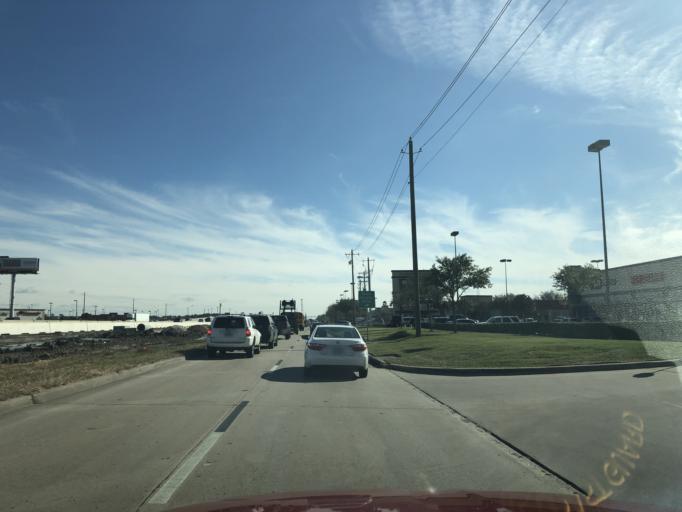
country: US
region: Texas
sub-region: Galveston County
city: League City
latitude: 29.4702
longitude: -95.0946
